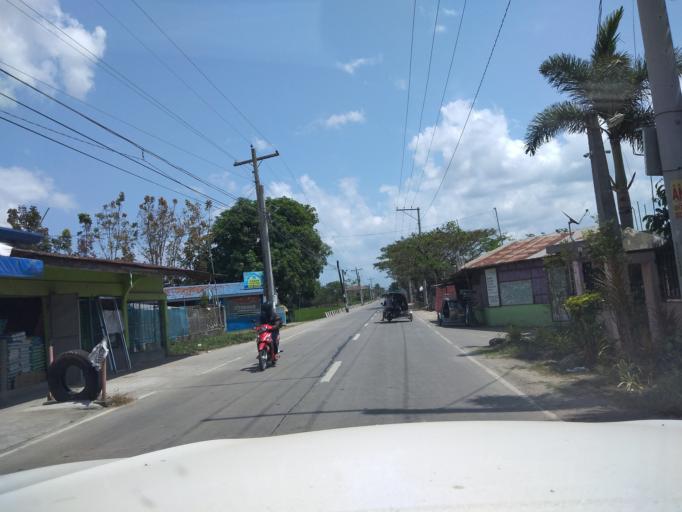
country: PH
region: Central Luzon
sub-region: Province of Pampanga
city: Lourdes
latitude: 15.0185
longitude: 120.8665
